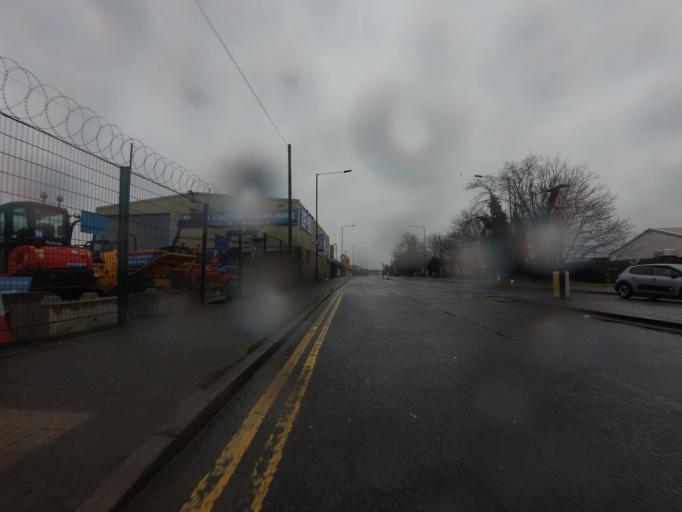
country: GB
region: England
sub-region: Hertfordshire
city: Waltham Cross
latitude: 51.6578
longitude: -0.0299
